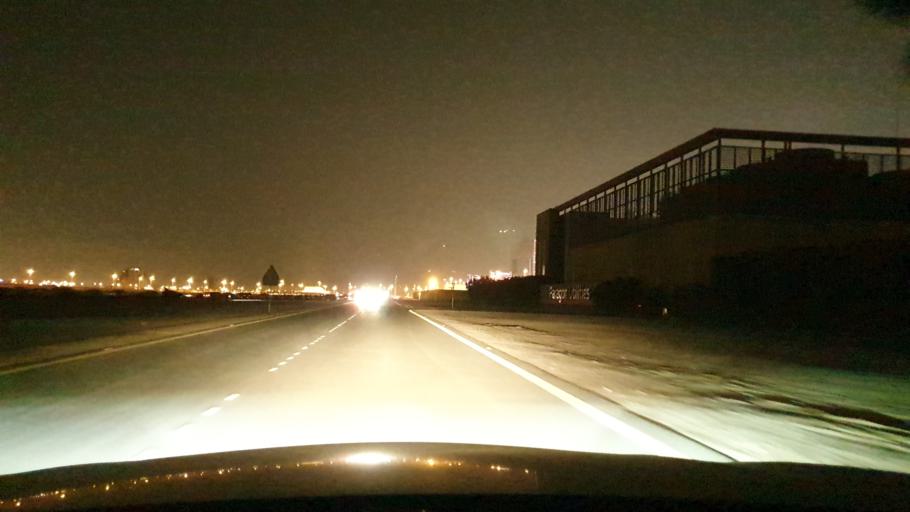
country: BH
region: Muharraq
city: Al Muharraq
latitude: 26.2552
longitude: 50.5830
